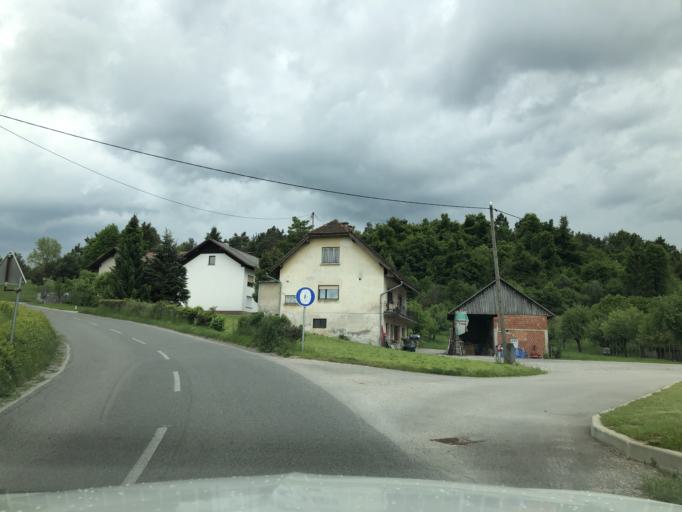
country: SI
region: Cerknica
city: Rakek
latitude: 45.8178
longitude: 14.2904
